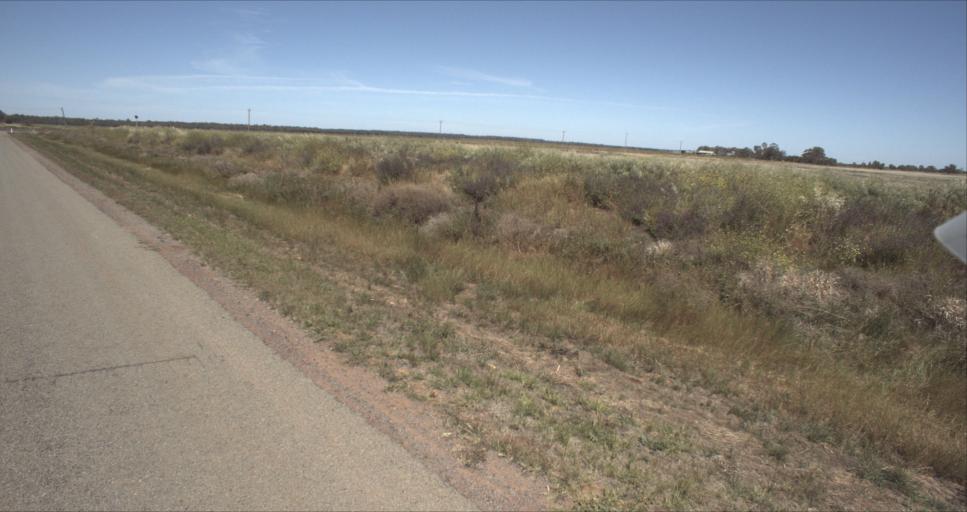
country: AU
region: New South Wales
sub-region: Leeton
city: Leeton
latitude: -34.5819
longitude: 146.3086
